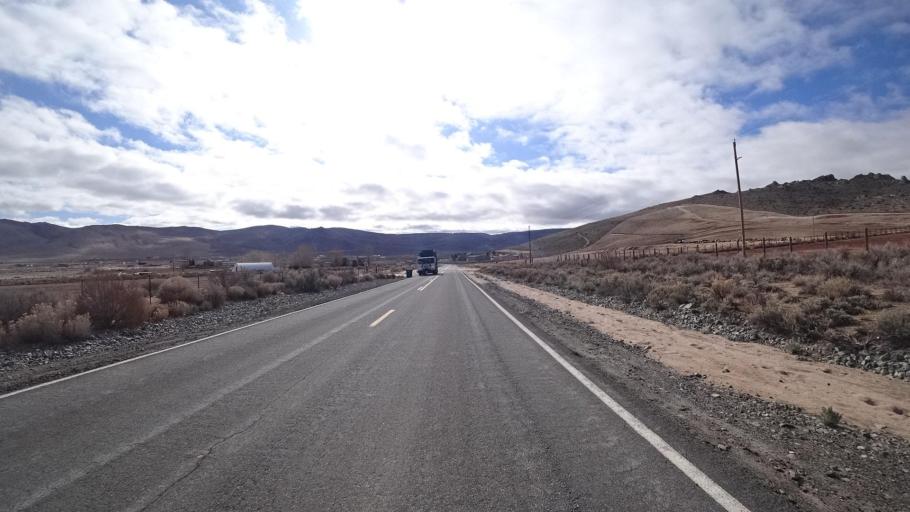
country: US
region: Nevada
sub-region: Washoe County
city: Cold Springs
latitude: 39.8646
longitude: -119.9427
